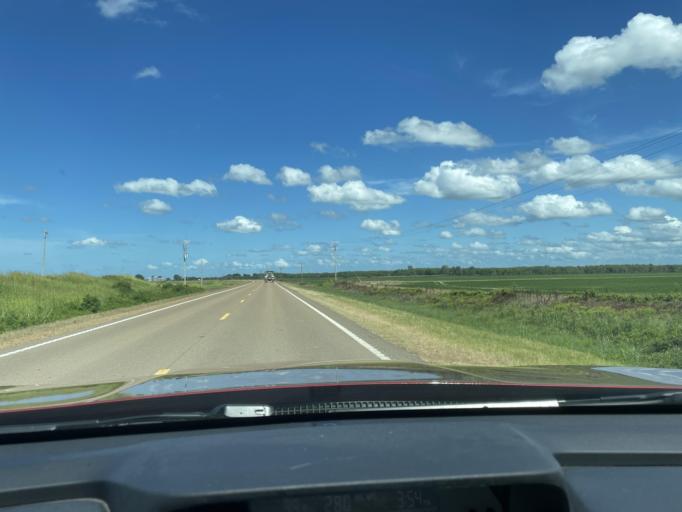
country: US
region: Mississippi
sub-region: Humphreys County
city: Belzoni
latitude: 33.1838
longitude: -90.6600
